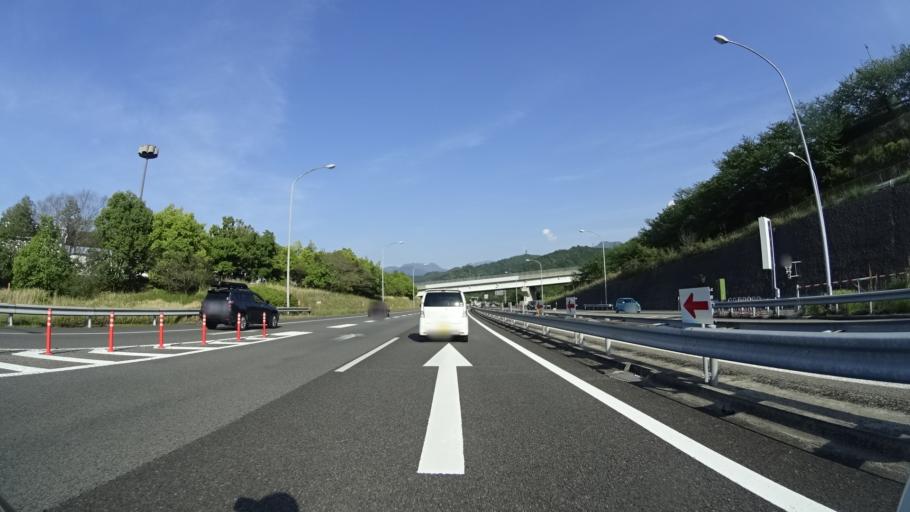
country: JP
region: Ehime
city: Saijo
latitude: 33.8853
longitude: 133.1088
